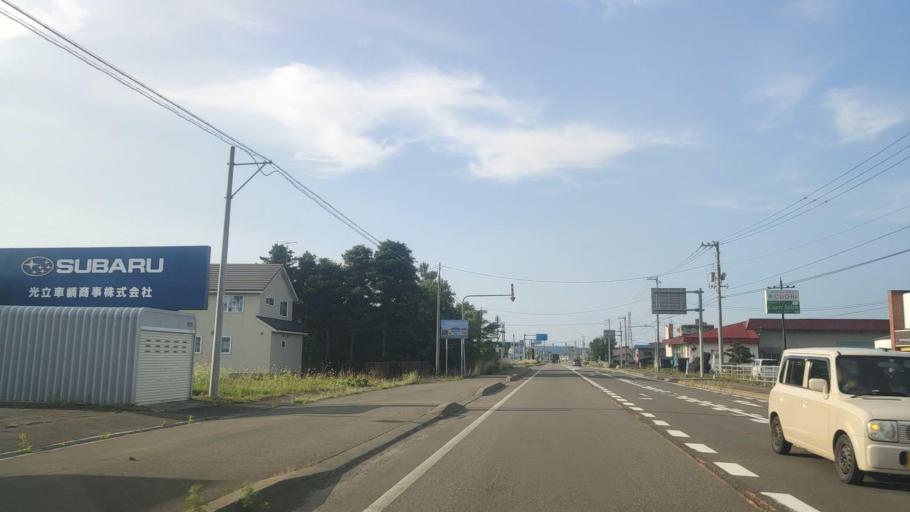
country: JP
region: Hokkaido
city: Iwamizawa
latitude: 43.0085
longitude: 141.7895
